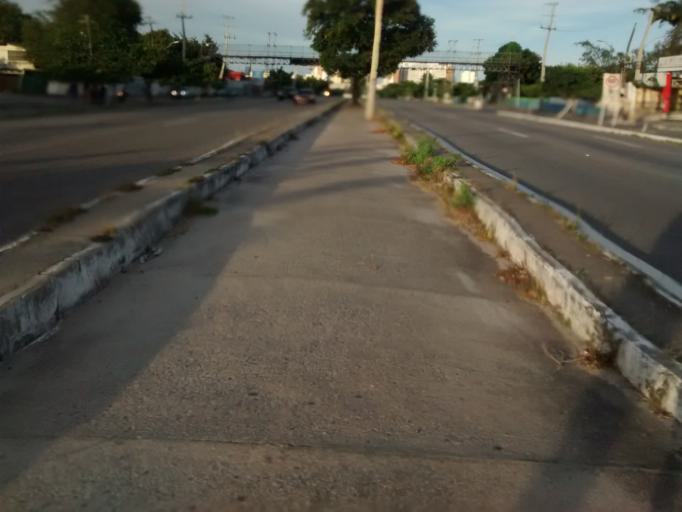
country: BR
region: Ceara
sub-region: Fortaleza
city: Fortaleza
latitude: -3.7381
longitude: -38.5802
